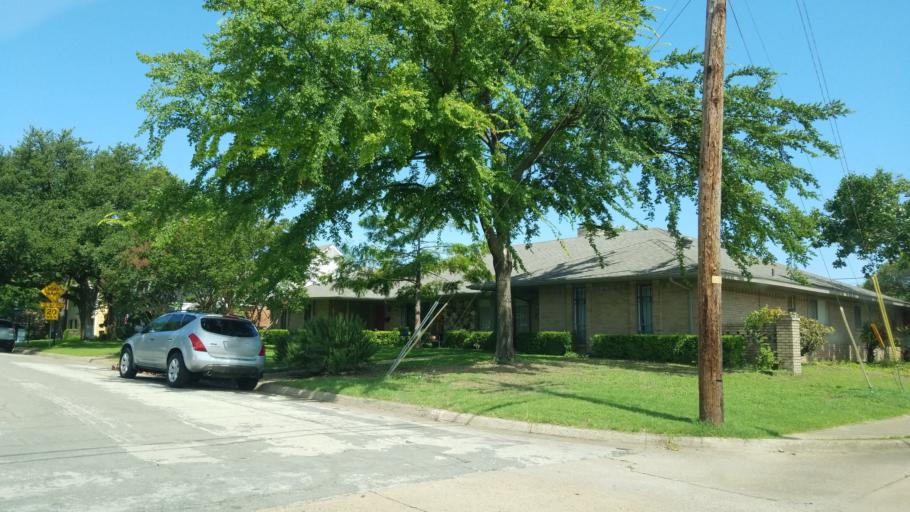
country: US
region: Texas
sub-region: Dallas County
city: Farmers Branch
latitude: 32.9075
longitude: -96.8515
